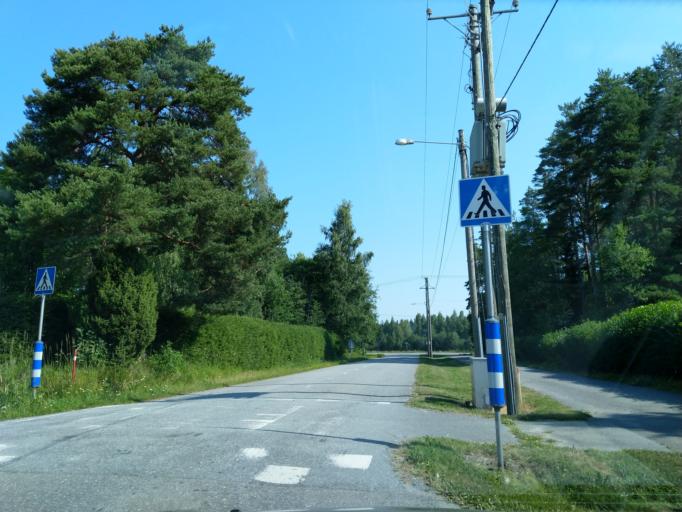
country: FI
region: Satakunta
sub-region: Pori
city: Noormarkku
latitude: 61.5848
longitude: 21.8977
